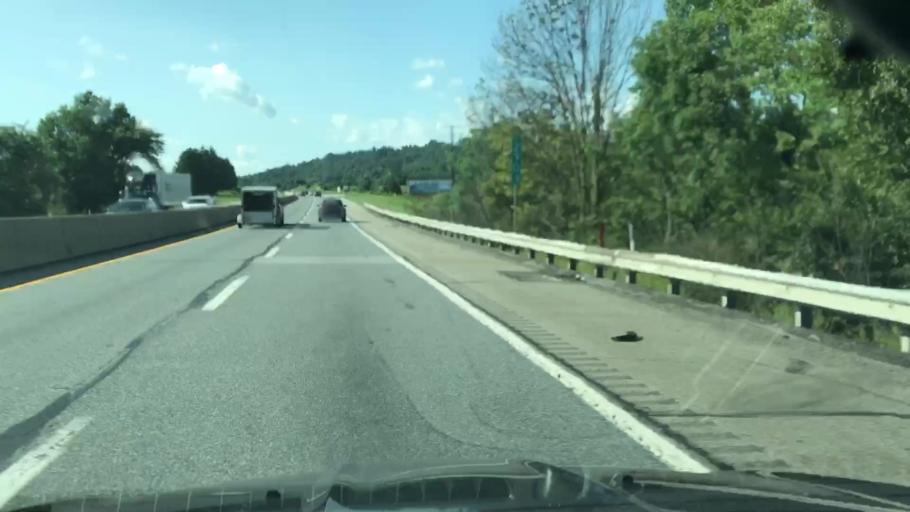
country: US
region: Pennsylvania
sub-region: Lancaster County
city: Bowmansville
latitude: 40.1913
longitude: -76.0030
